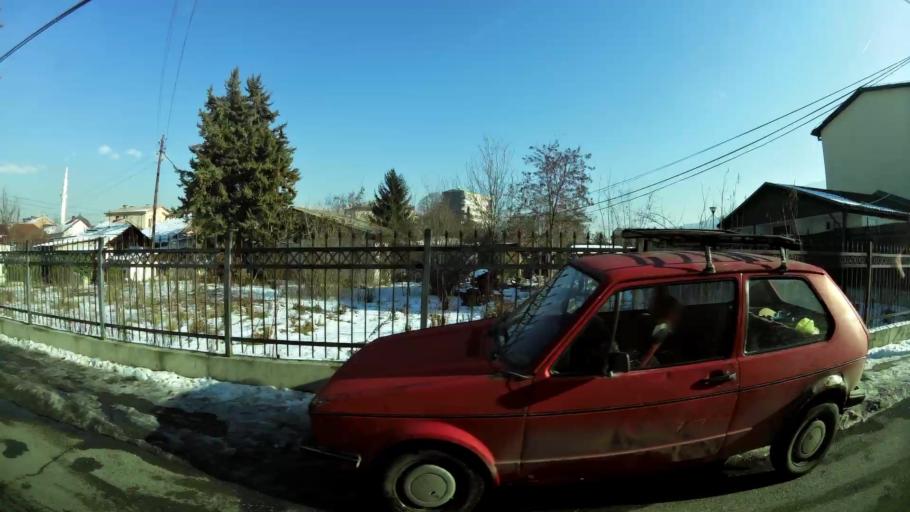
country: MK
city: Krushopek
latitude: 42.0023
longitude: 21.3818
